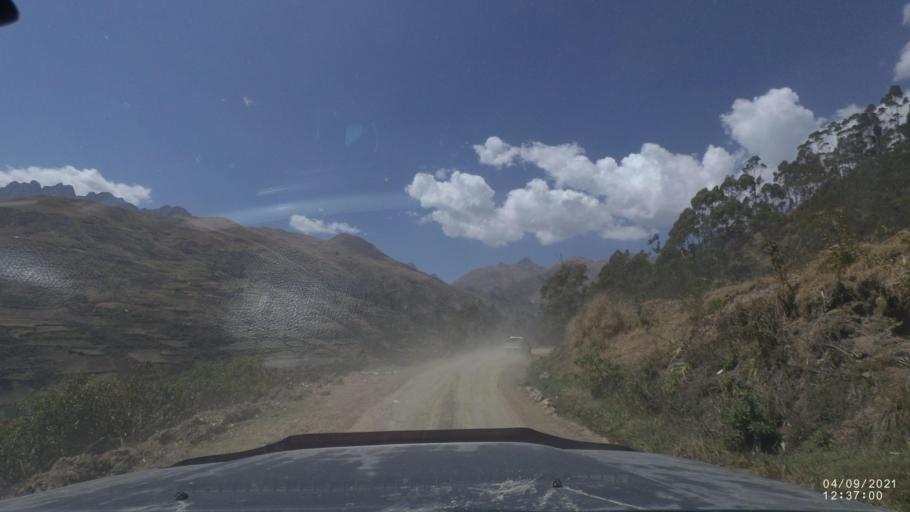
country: BO
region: Cochabamba
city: Colchani
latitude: -17.2263
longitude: -66.5051
